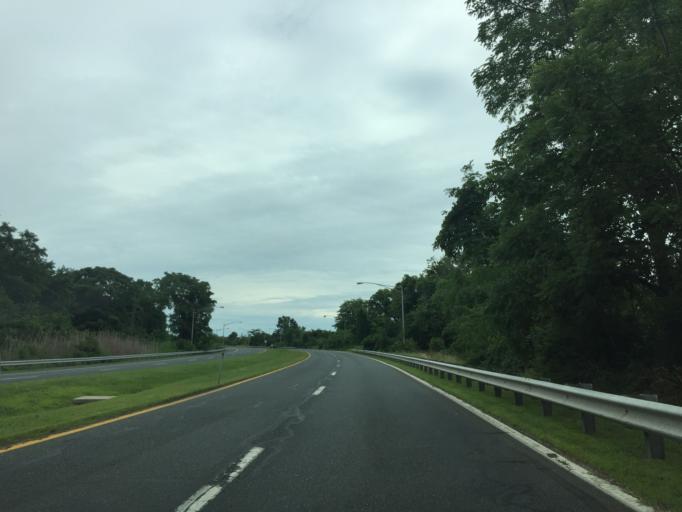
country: US
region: Maryland
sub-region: Baltimore County
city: Dundalk
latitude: 39.2516
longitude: -76.4986
